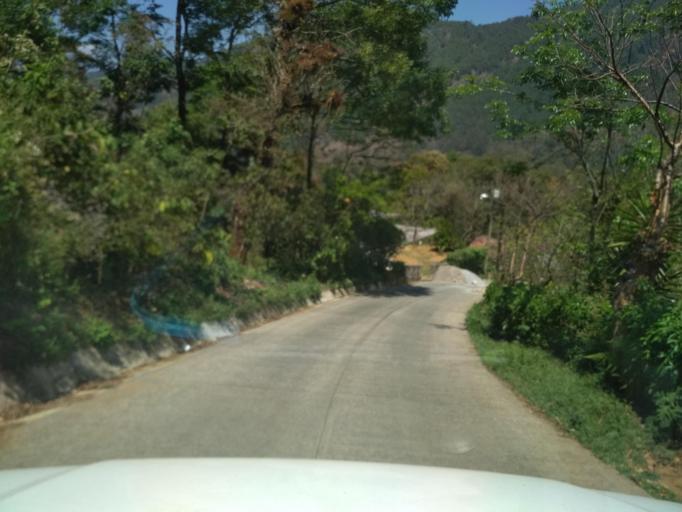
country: MX
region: Veracruz
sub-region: Tlilapan
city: Tonalixco
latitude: 18.7781
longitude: -97.0788
